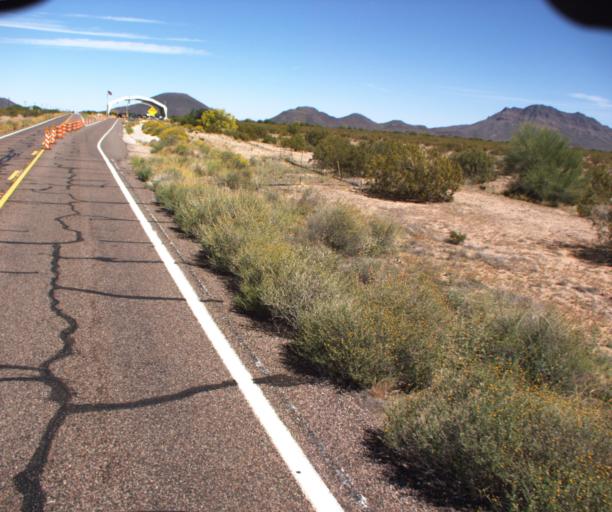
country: US
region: Arizona
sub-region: Maricopa County
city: Gila Bend
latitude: 32.7121
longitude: -112.8435
